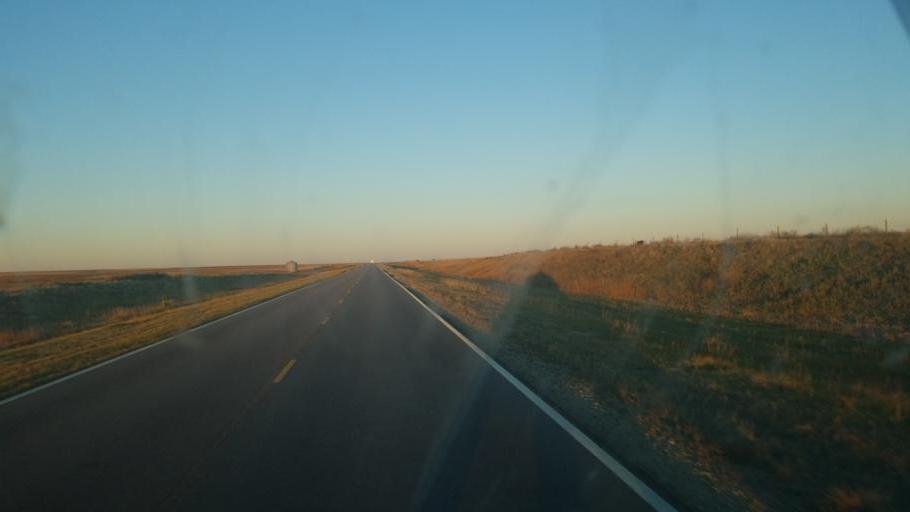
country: US
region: Kansas
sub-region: Wallace County
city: Sharon Springs
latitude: 38.9012
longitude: -101.8196
